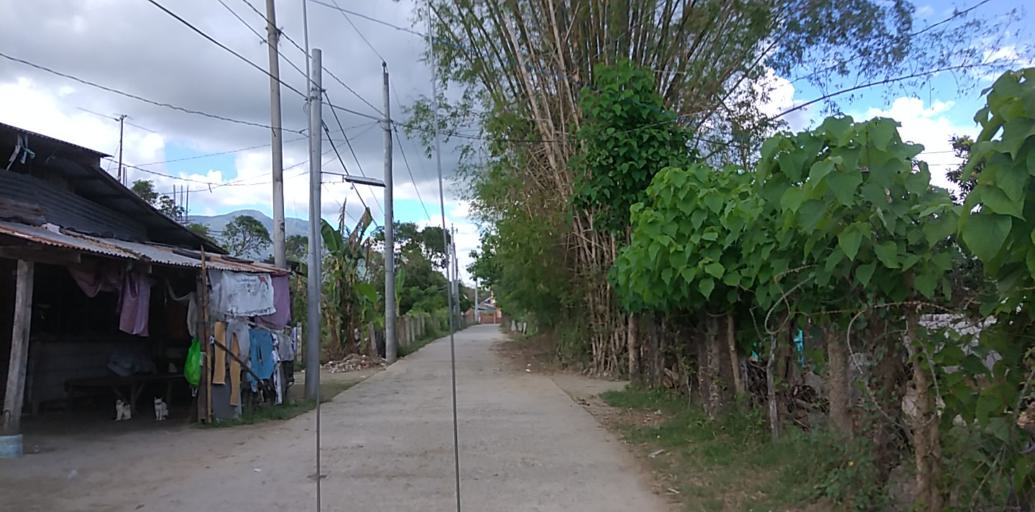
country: PH
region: Central Luzon
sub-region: Province of Pampanga
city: Arayat
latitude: 15.1365
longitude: 120.7821
